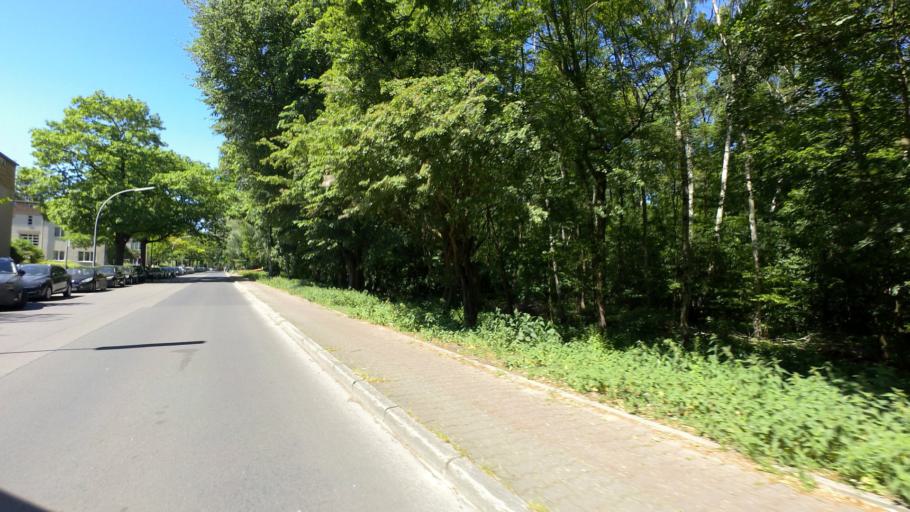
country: DE
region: Berlin
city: Siemensstadt
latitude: 52.5411
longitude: 13.2796
